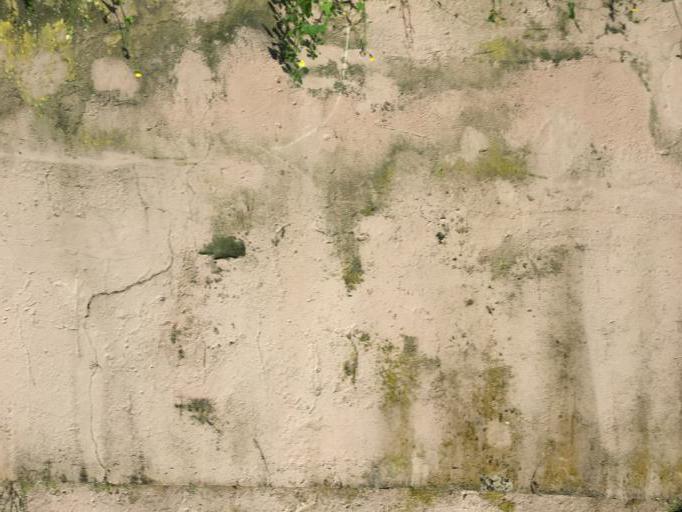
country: PT
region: Lisbon
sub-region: Sintra
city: Sintra
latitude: 38.8071
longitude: -9.3980
